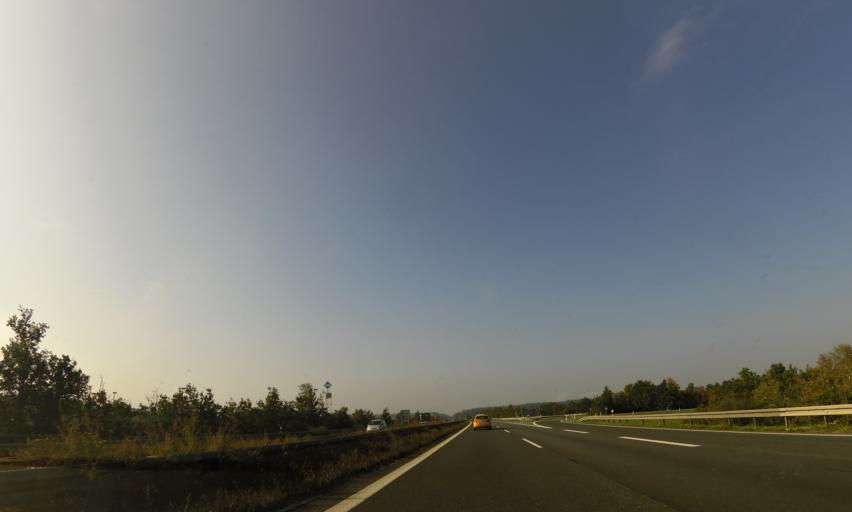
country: DE
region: Bavaria
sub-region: Regierungsbezirk Mittelfranken
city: Herrieden
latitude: 49.2608
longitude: 10.5035
